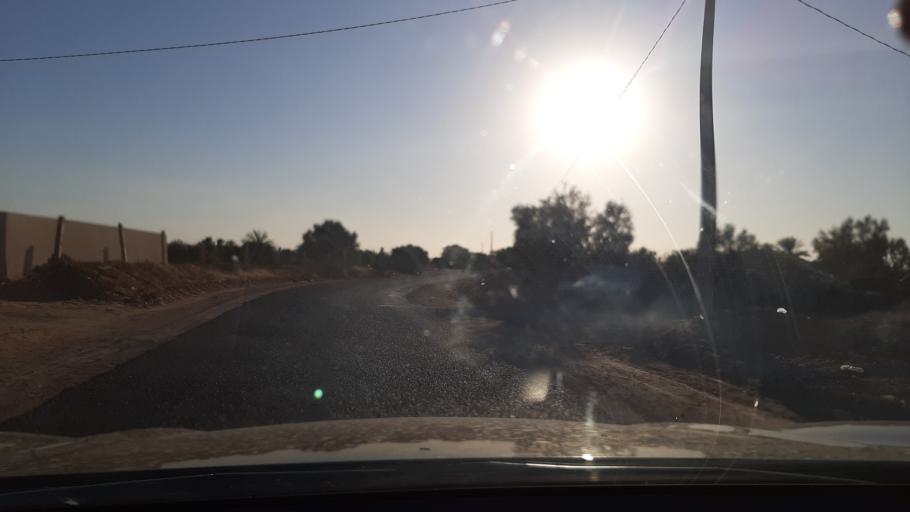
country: TN
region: Qabis
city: Matmata
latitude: 33.6176
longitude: 10.2566
